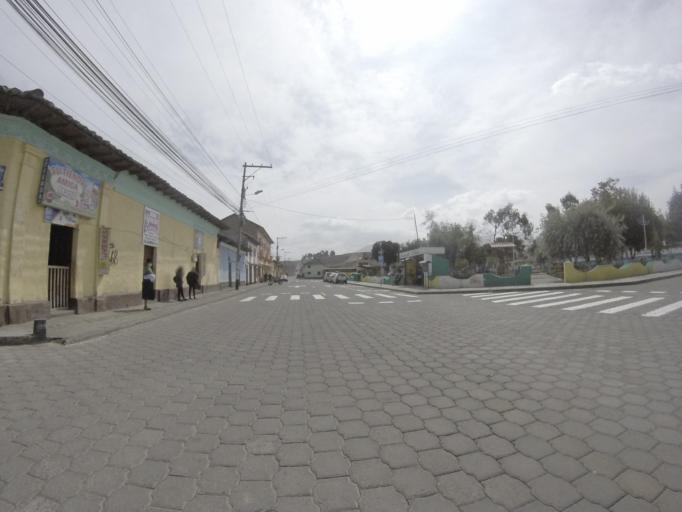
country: EC
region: Pichincha
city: Cayambe
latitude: 0.1386
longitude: -78.0806
